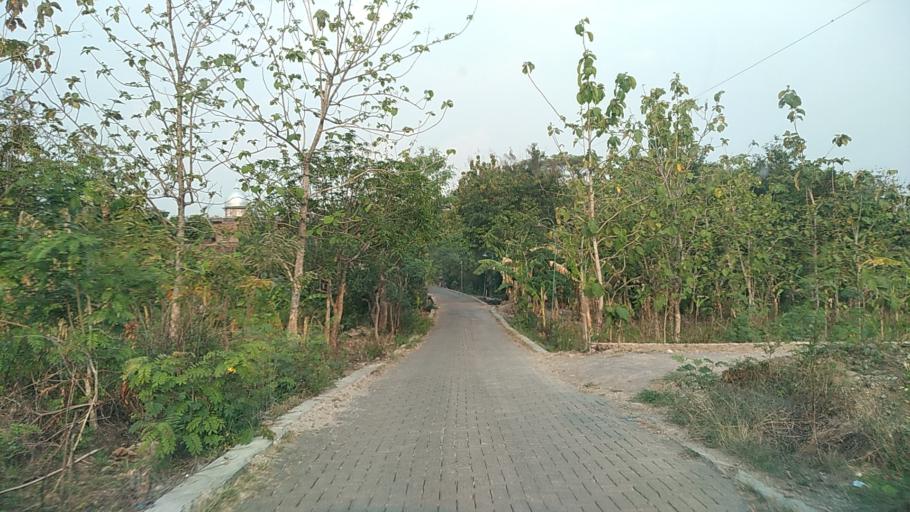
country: ID
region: Central Java
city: Mranggen
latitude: -7.0689
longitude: 110.4828
